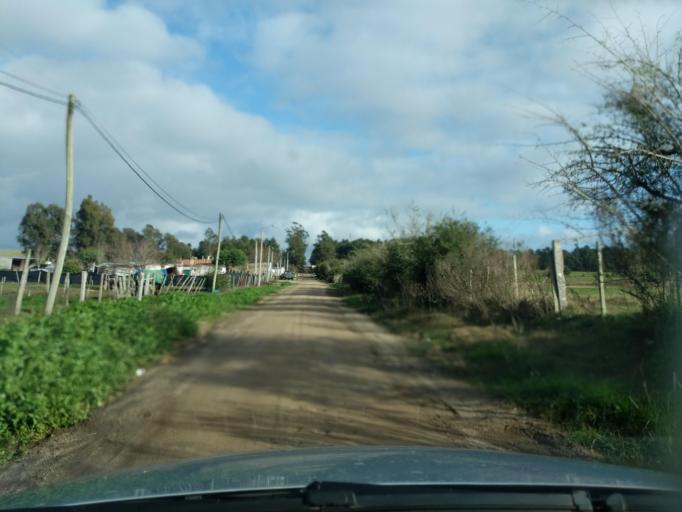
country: UY
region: Florida
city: Florida
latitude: -34.0767
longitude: -56.2261
